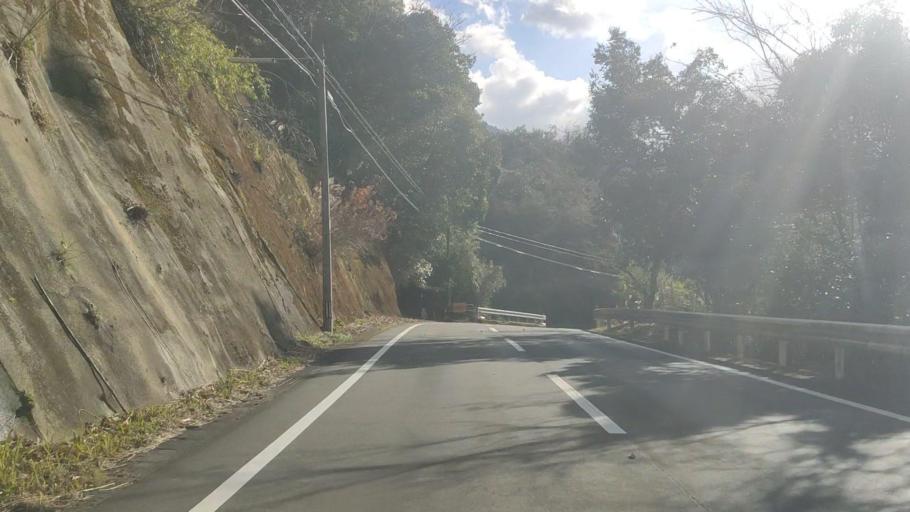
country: JP
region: Kumamoto
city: Hitoyoshi
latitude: 32.3189
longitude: 130.8429
